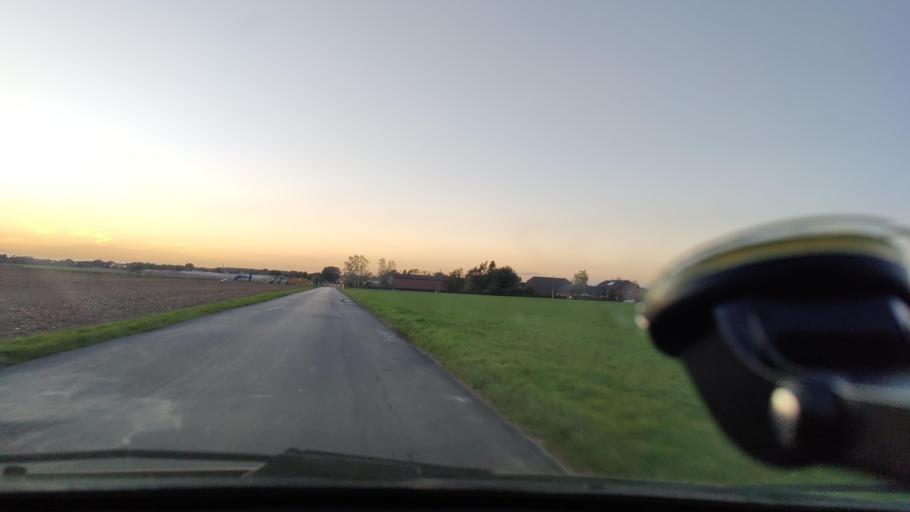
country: DE
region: North Rhine-Westphalia
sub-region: Regierungsbezirk Dusseldorf
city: Goch
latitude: 51.7121
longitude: 6.1873
